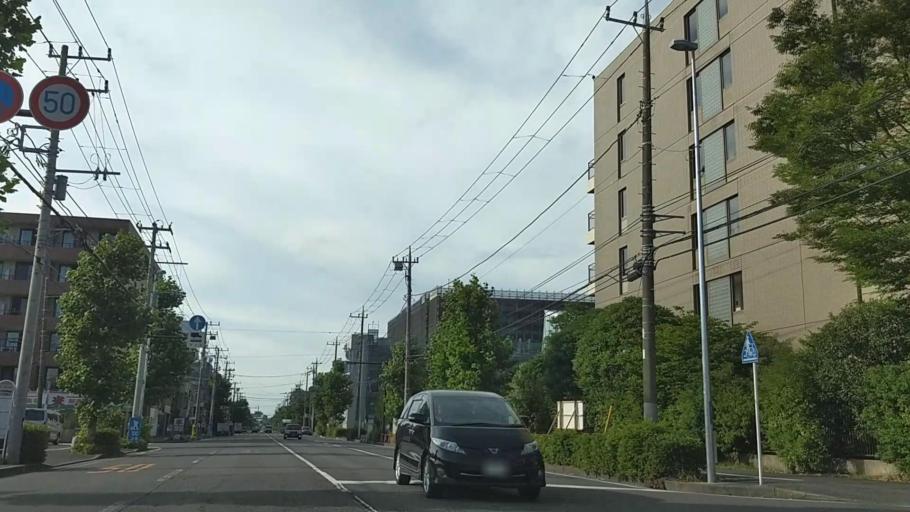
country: JP
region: Kanagawa
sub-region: Kawasaki-shi
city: Kawasaki
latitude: 35.5053
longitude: 139.6934
